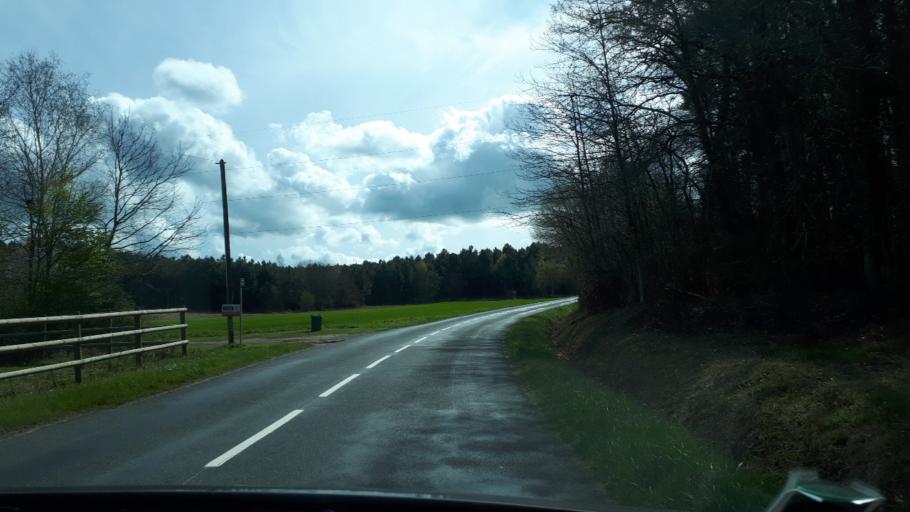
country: FR
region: Pays de la Loire
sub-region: Departement de la Sarthe
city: Brette-les-Pins
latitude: 47.8679
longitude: 0.3546
